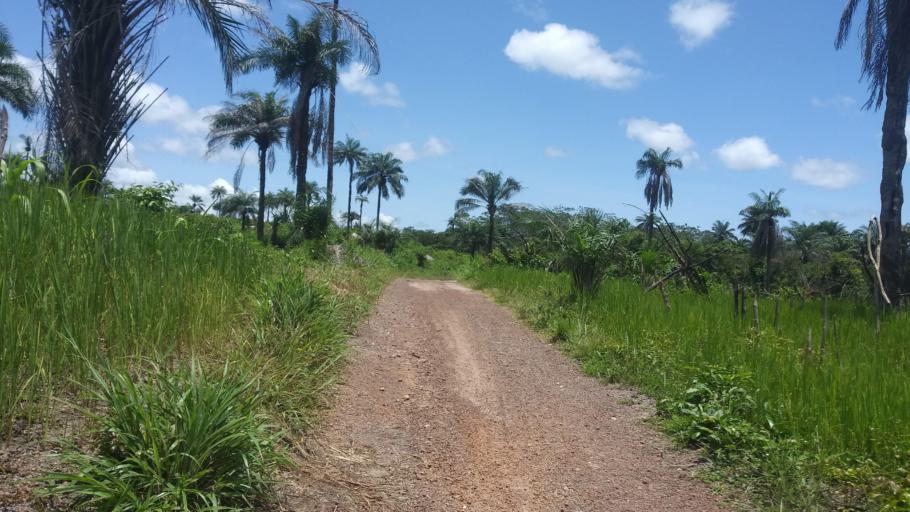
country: SL
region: Northern Province
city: Makeni
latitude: 8.8940
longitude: -12.0035
